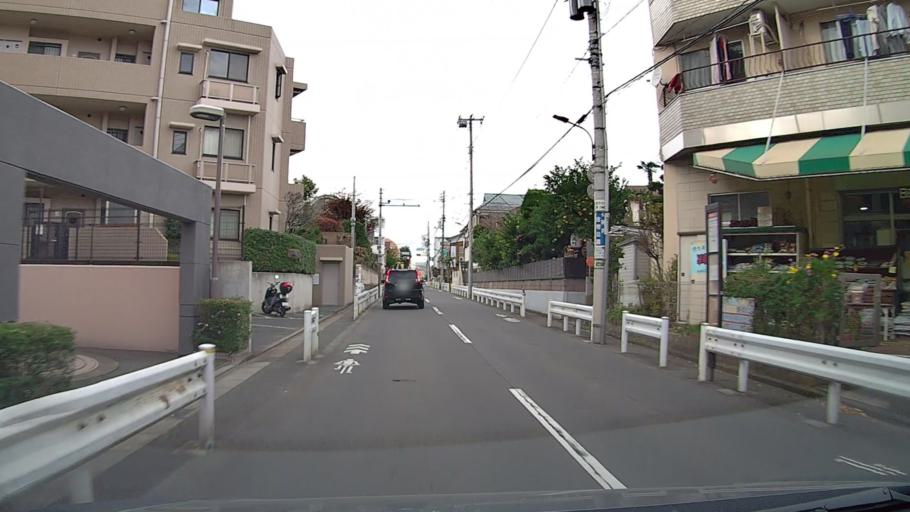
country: JP
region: Saitama
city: Wako
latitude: 35.7279
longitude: 139.6189
